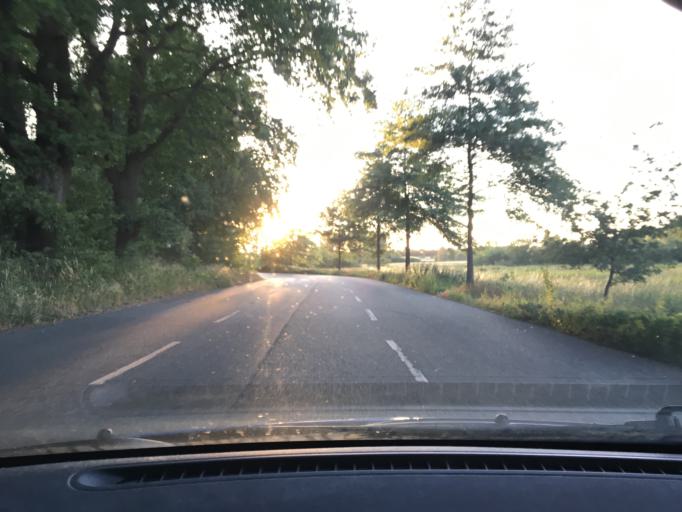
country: DE
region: Lower Saxony
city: Uelzen
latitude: 52.9862
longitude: 10.5654
